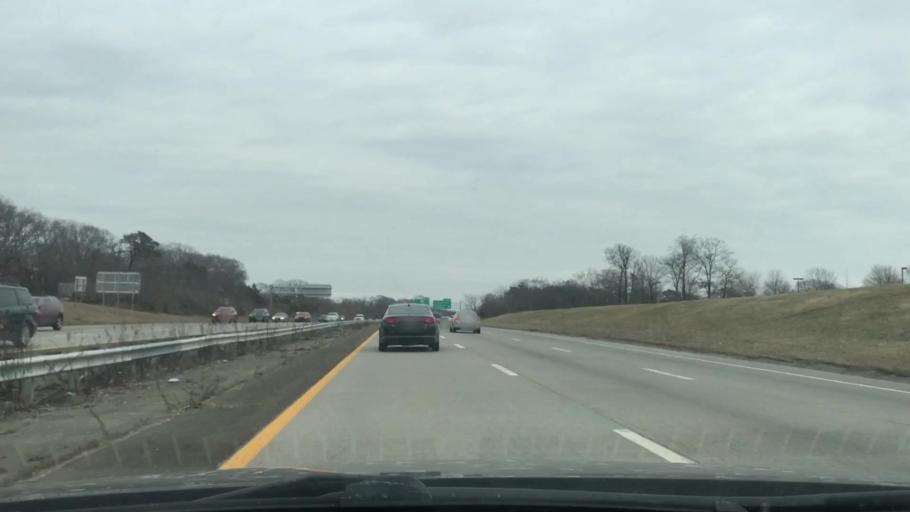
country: US
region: New York
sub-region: Suffolk County
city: Patchogue
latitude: 40.7775
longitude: -73.0288
